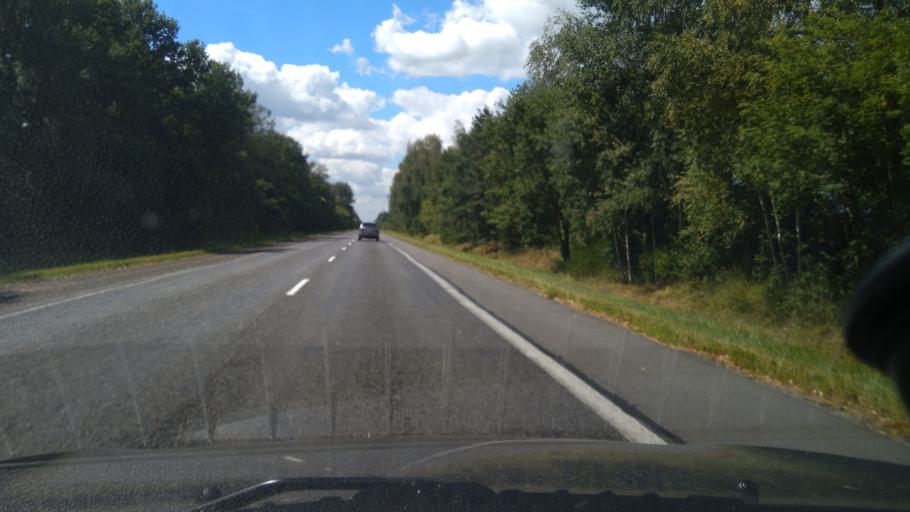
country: BY
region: Brest
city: Ivatsevichy
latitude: 52.6778
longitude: 25.2739
